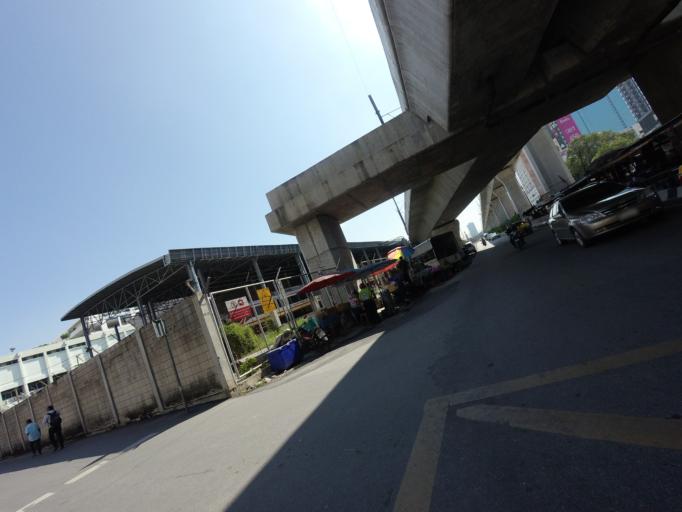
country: TH
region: Bangkok
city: Watthana
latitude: 13.7455
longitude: 100.5849
